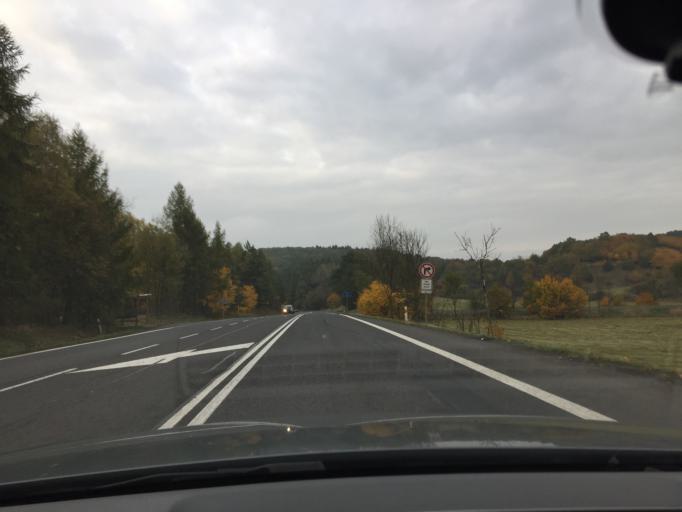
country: CZ
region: Ustecky
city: Velemin
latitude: 50.5671
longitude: 13.9575
